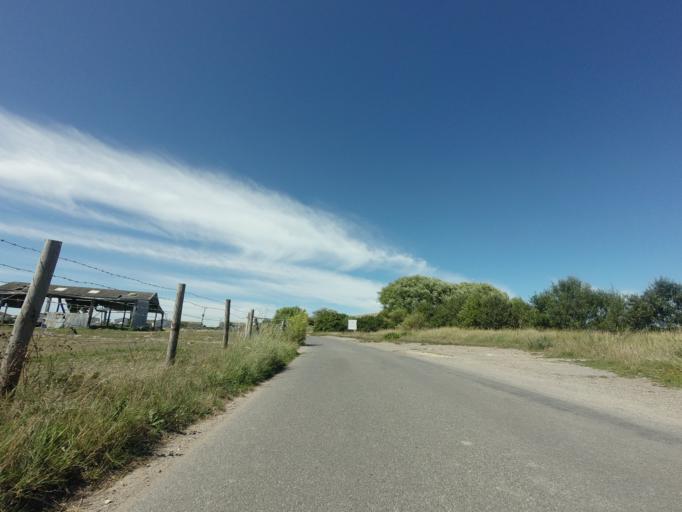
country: GB
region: England
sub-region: Kent
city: Deal
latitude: 51.2500
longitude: 1.3929
